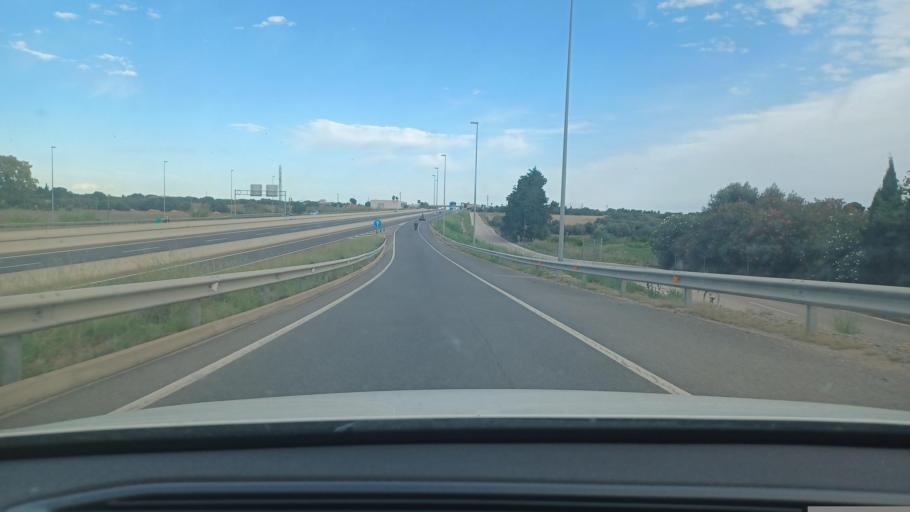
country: ES
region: Catalonia
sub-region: Provincia de Tarragona
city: Cambrils
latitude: 41.0841
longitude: 1.0793
